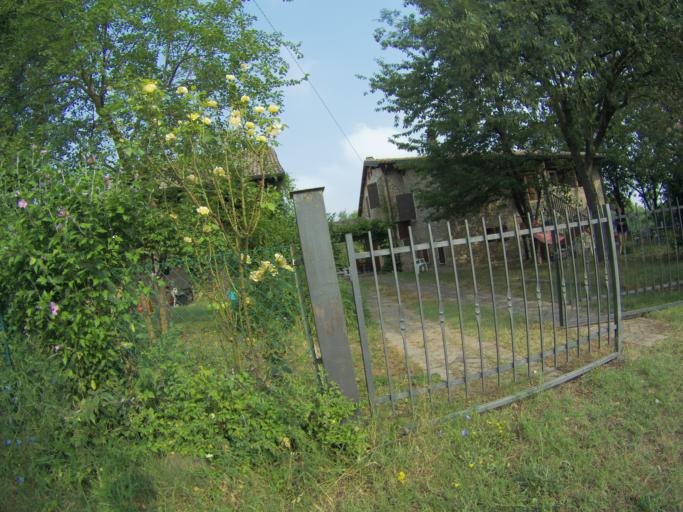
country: IT
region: Emilia-Romagna
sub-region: Provincia di Reggio Emilia
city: Albinea
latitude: 44.6213
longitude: 10.6255
